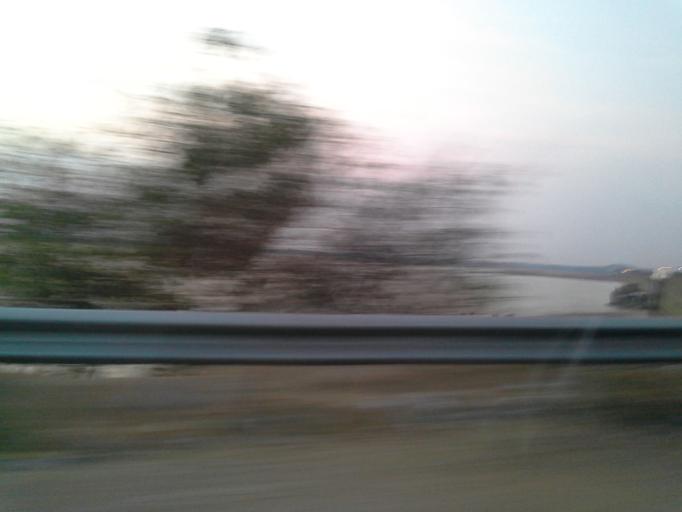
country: IN
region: Telangana
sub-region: Hyderabad
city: Hyderabad
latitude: 17.3207
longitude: 78.3710
